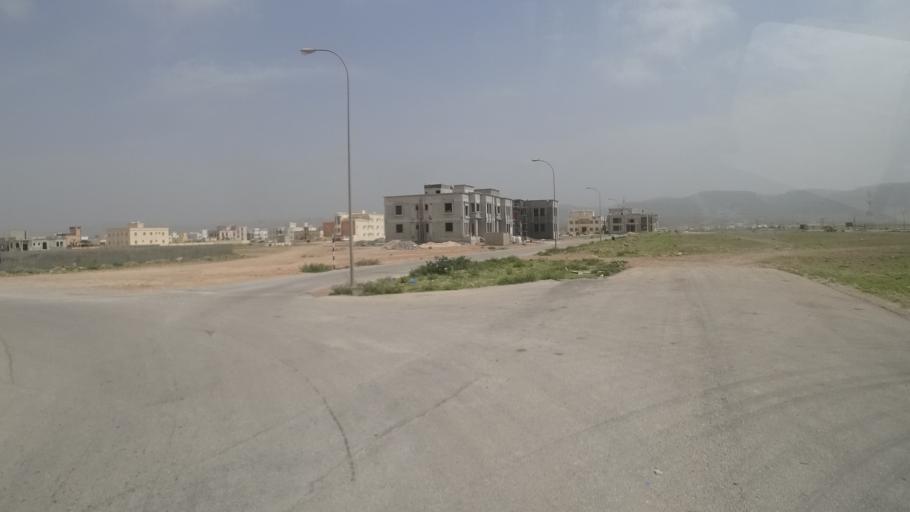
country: OM
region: Zufar
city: Salalah
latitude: 17.0977
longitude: 54.2159
